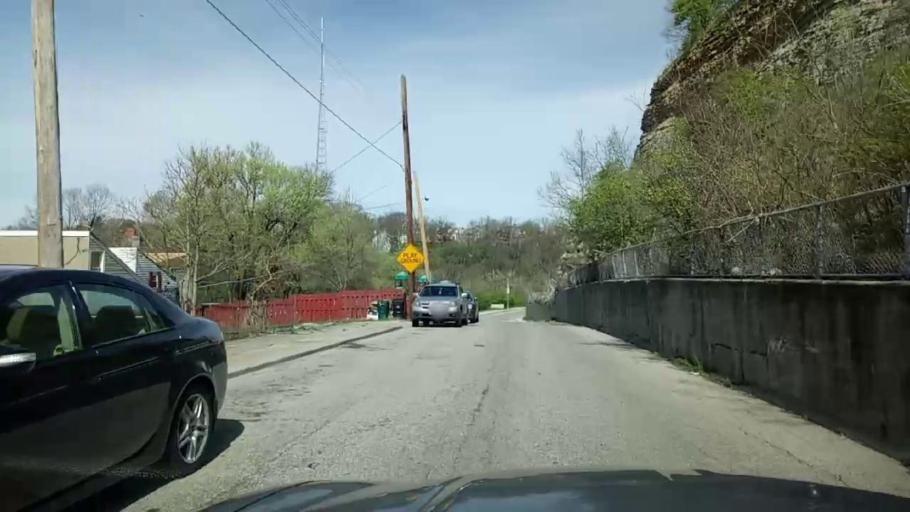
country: US
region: Kentucky
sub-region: Campbell County
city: Newport
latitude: 39.1203
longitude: -84.5131
